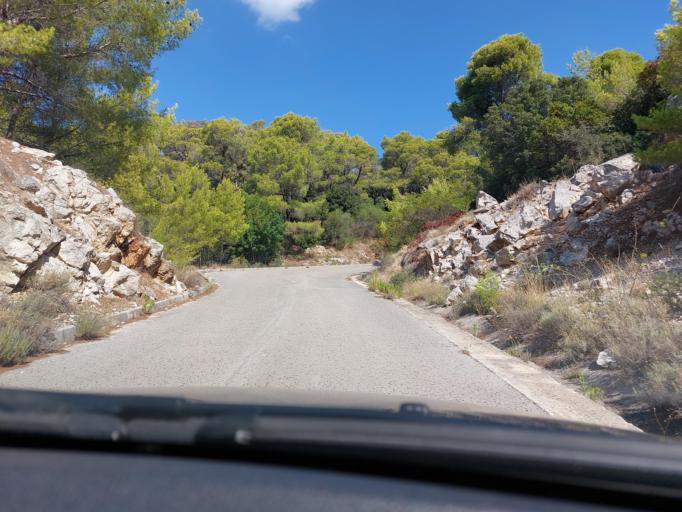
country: HR
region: Dubrovacko-Neretvanska
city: Smokvica
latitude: 42.7487
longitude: 16.8437
